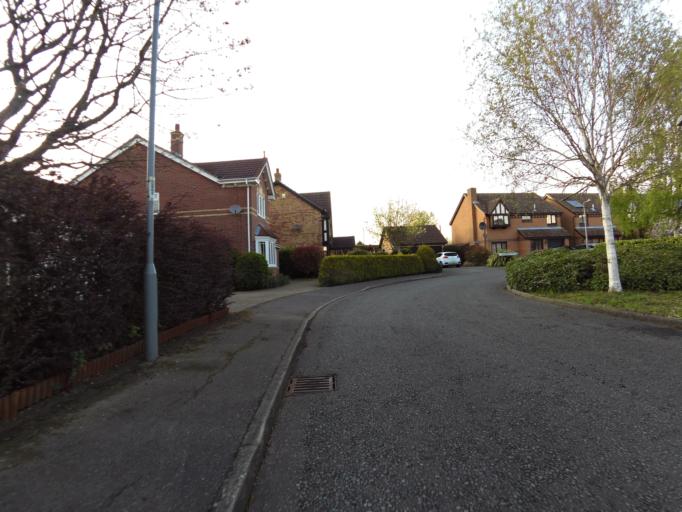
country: GB
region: England
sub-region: Suffolk
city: Ipswich
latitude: 52.0729
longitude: 1.1822
